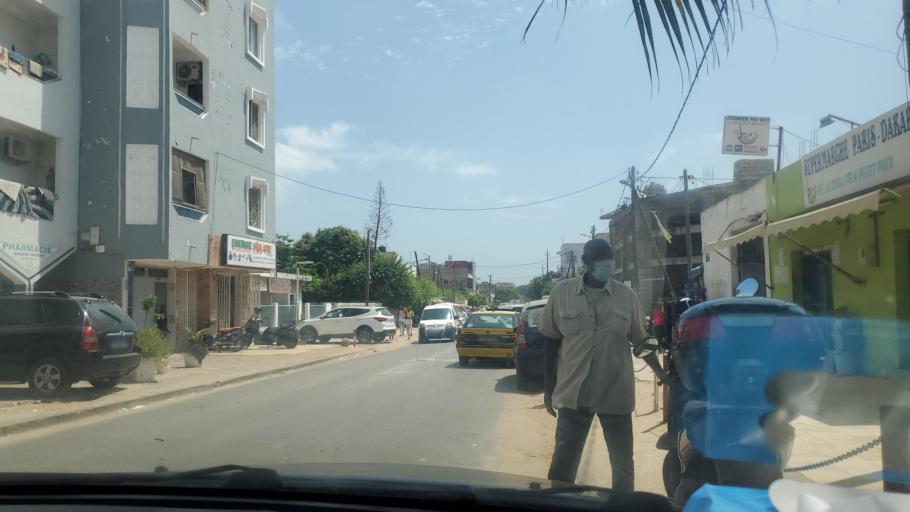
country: SN
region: Dakar
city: Grand Dakar
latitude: 14.7260
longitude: -17.4504
